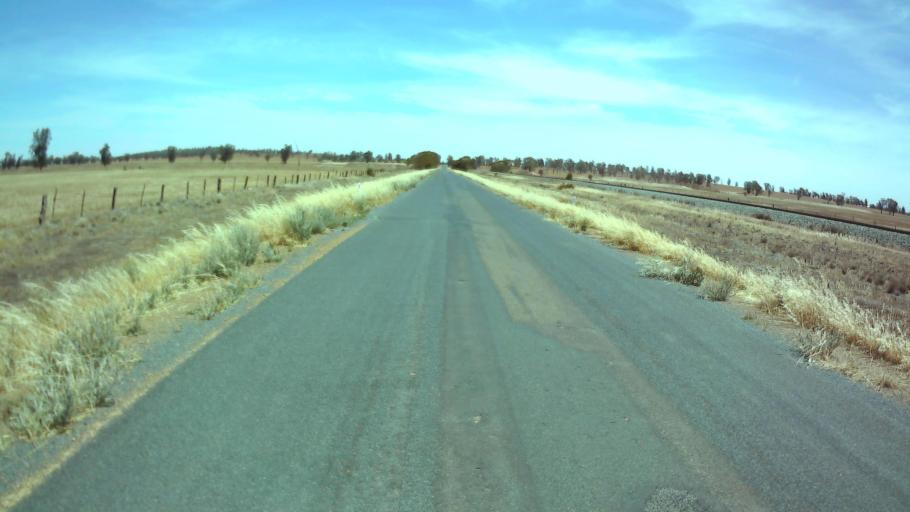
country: AU
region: New South Wales
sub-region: Weddin
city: Grenfell
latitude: -33.7603
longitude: 147.7613
